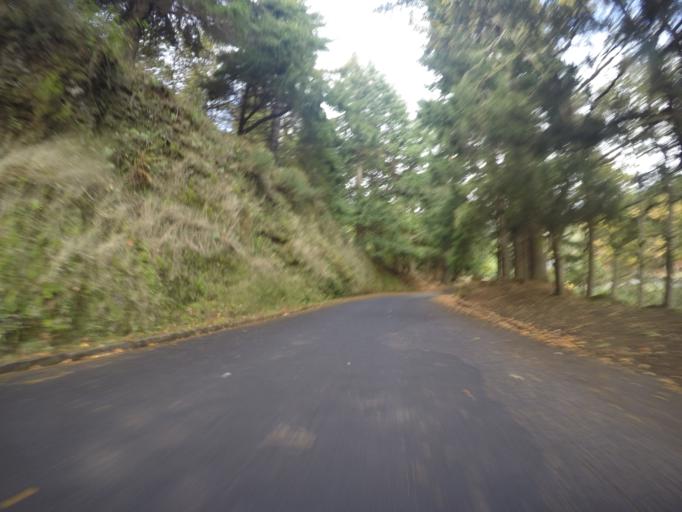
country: PT
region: Madeira
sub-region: Funchal
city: Nossa Senhora do Monte
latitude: 32.6979
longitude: -16.8841
